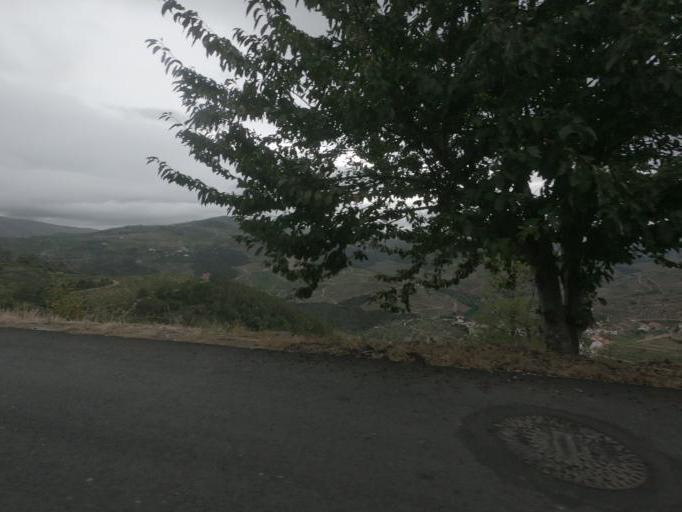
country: PT
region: Vila Real
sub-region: Sabrosa
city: Sabrosa
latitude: 41.2147
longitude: -7.5285
